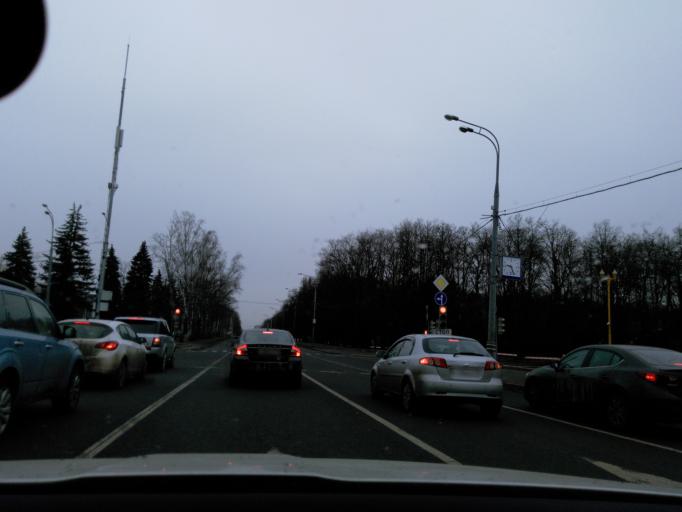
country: RU
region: Moscow
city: Vorob'yovo
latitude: 55.7059
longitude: 37.5362
